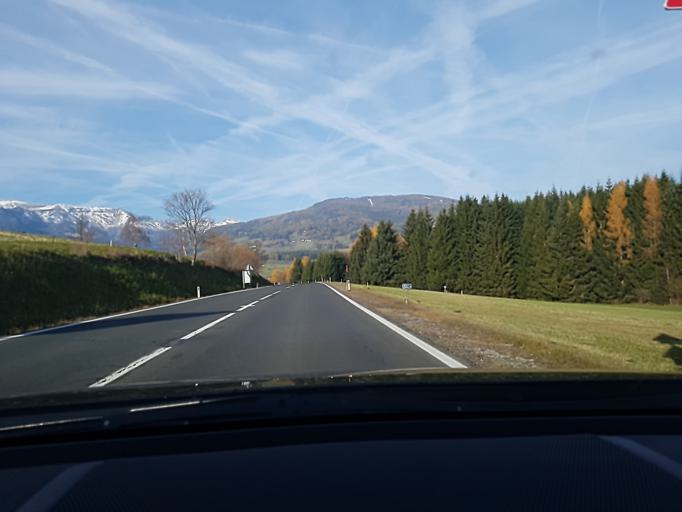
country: AT
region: Salzburg
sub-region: Politischer Bezirk Tamsweg
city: Mariapfarr
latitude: 47.1412
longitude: 13.7344
